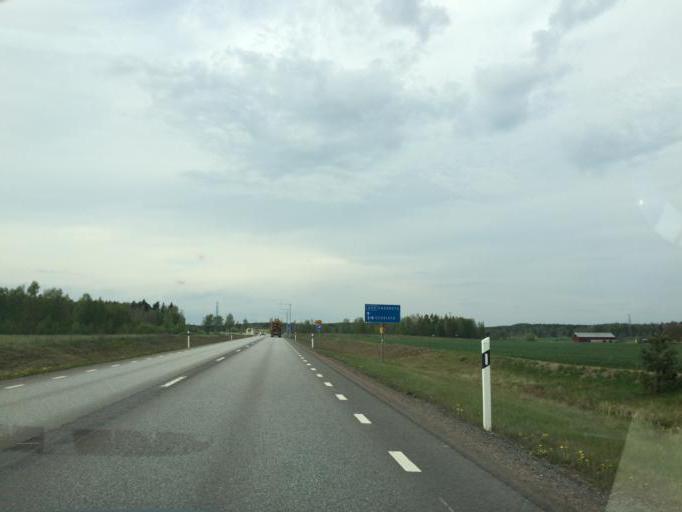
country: SE
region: Vaestmanland
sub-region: Kopings Kommun
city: Koping
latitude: 59.5326
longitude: 15.9562
